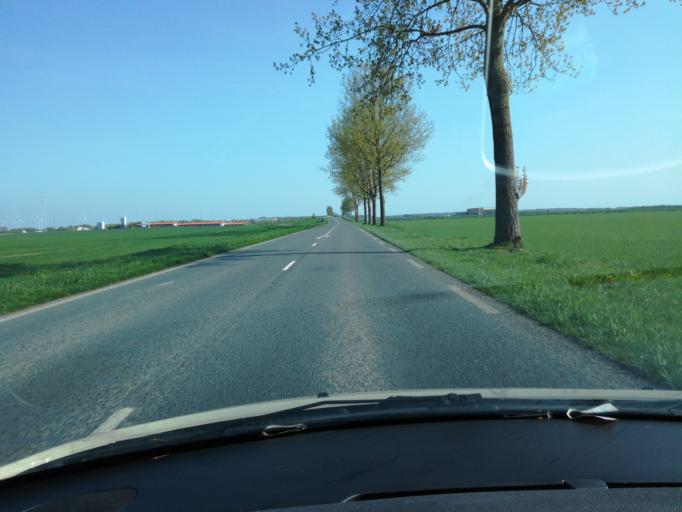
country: FR
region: Picardie
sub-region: Departement de la Somme
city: Poix-de-Picardie
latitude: 49.8138
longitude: 1.9620
